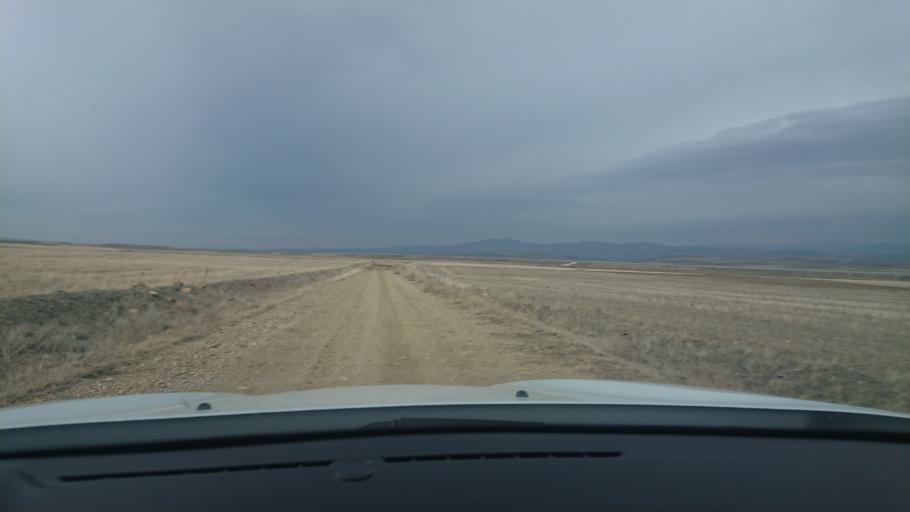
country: TR
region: Aksaray
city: Sariyahsi
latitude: 38.9807
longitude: 33.8787
